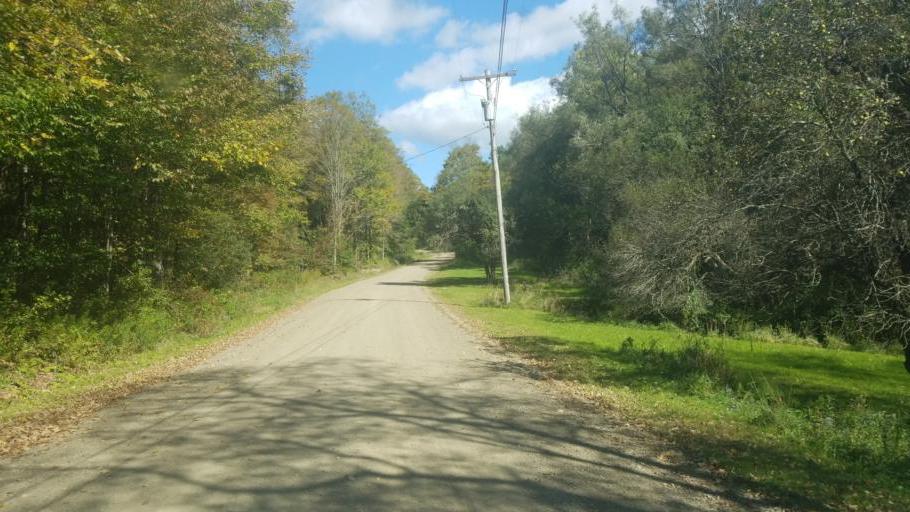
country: US
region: New York
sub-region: Allegany County
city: Cuba
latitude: 42.1705
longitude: -78.3329
